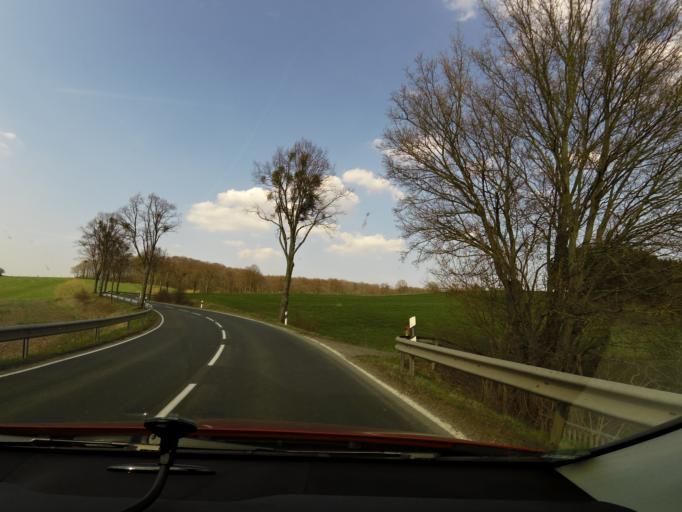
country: DE
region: Lower Saxony
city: Waake
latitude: 51.5972
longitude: 10.0297
